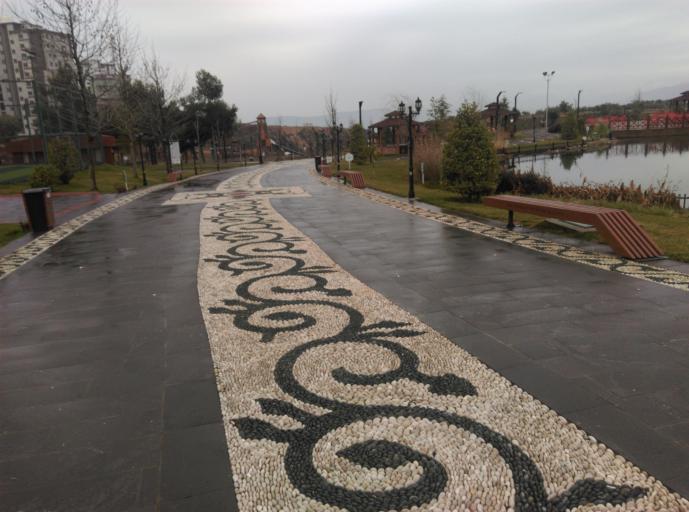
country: TR
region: Kahramanmaras
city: Kahramanmaras
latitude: 37.5824
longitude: 36.8902
